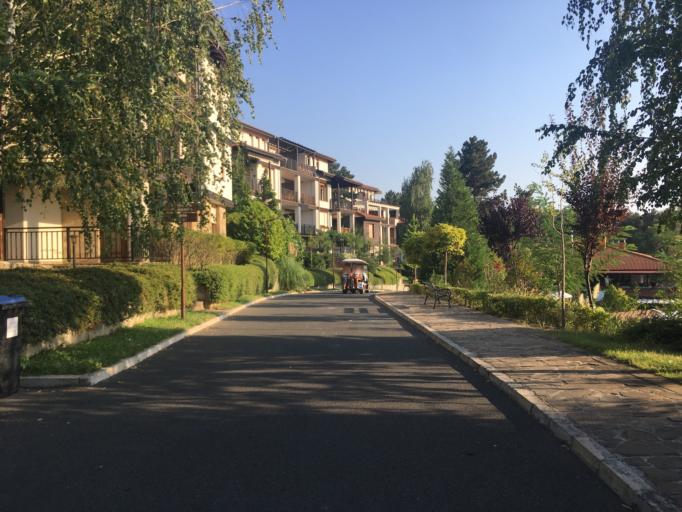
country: BG
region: Burgas
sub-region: Obshtina Sozopol
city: Sozopol
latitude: 42.4092
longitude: 27.6782
